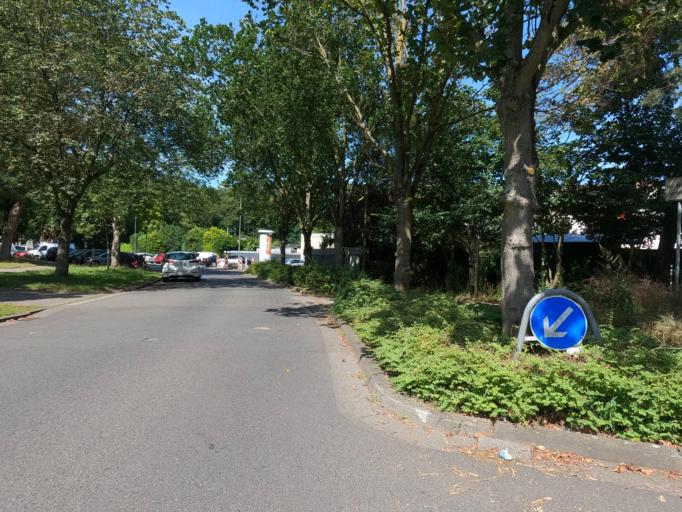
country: DE
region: Hesse
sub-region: Regierungsbezirk Darmstadt
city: Neu Isenburg
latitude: 50.0336
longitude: 8.6846
